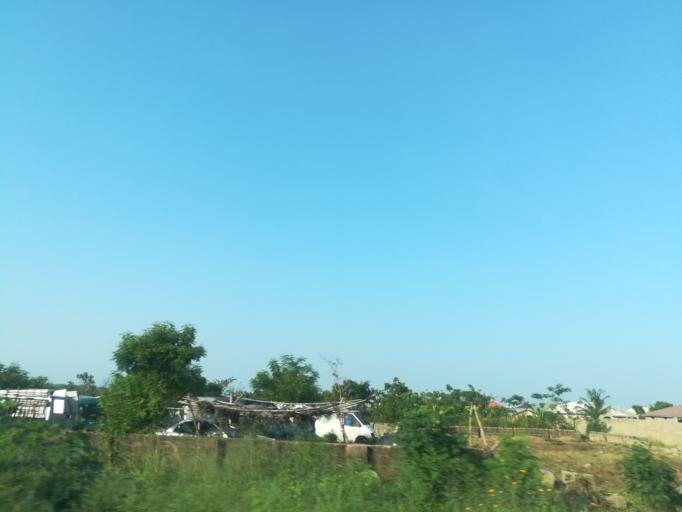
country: NG
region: Ogun
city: Abeokuta
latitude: 7.1838
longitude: 3.2754
